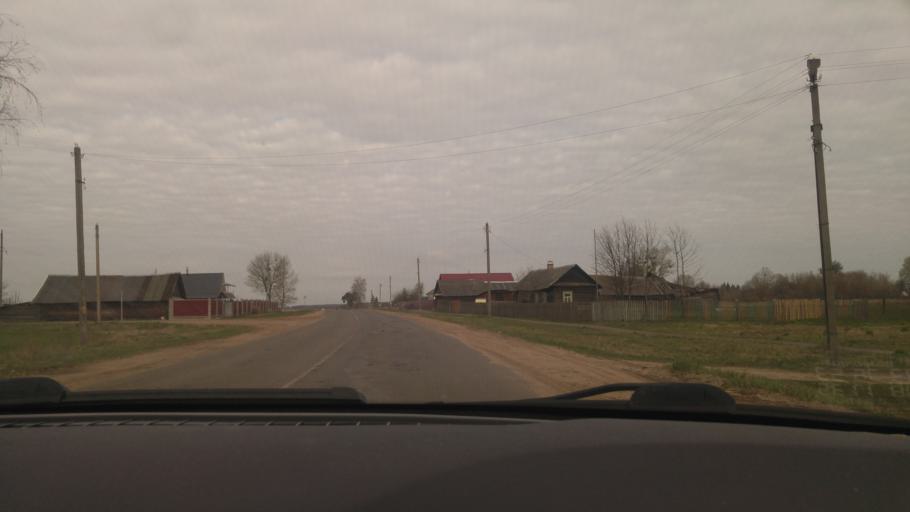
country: BY
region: Minsk
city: Chervyen'
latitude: 53.6495
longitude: 28.6210
